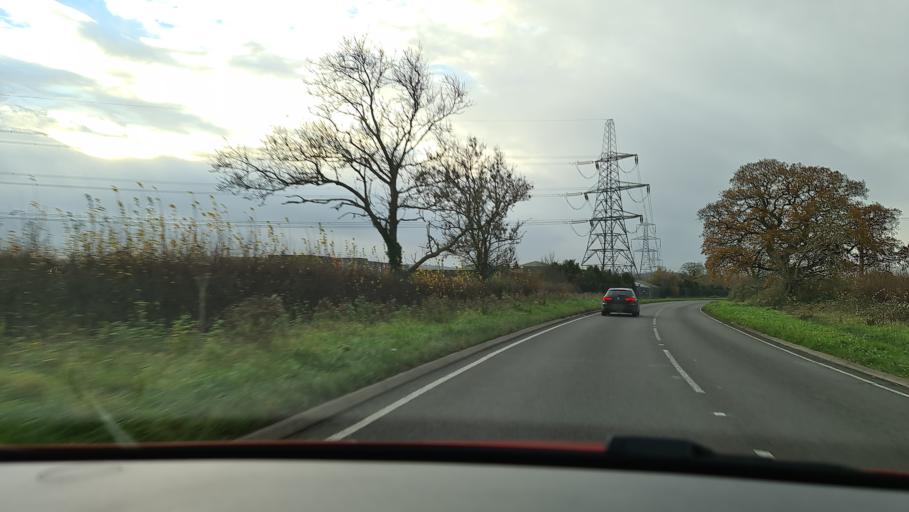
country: GB
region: England
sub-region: Oxfordshire
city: Bicester
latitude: 51.8585
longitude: -1.0892
